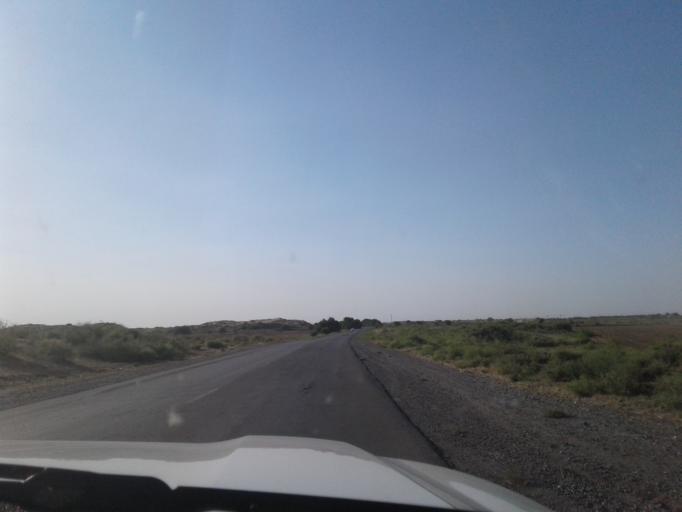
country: TM
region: Mary
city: Yoloeten
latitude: 37.1593
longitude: 62.4297
